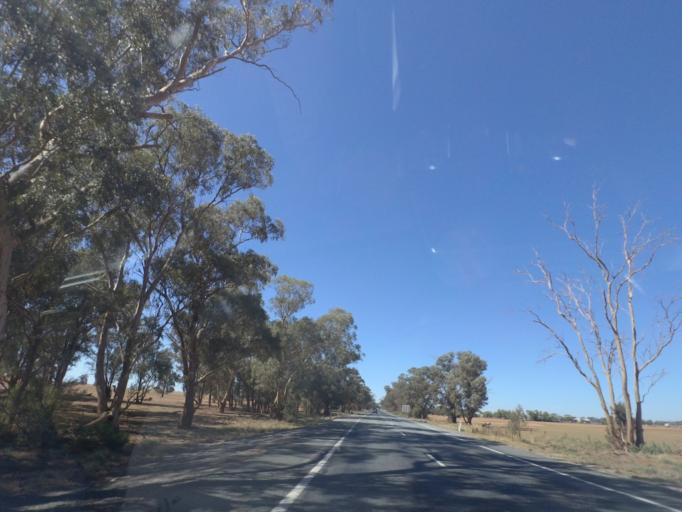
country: AU
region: New South Wales
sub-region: Bland
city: West Wyalong
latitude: -34.2035
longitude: 147.1099
